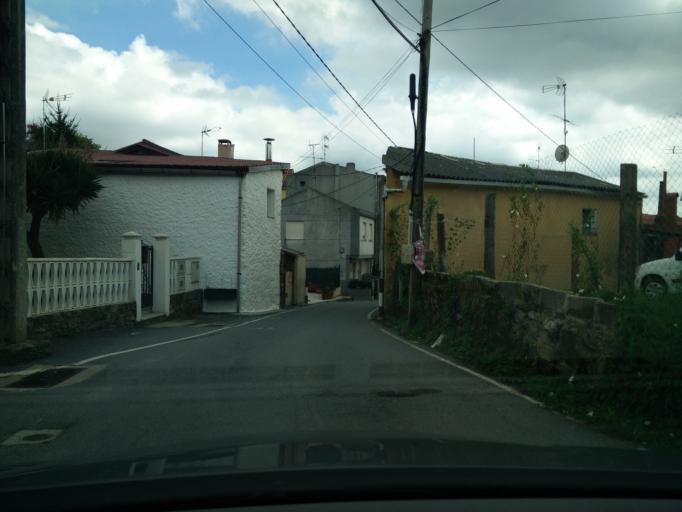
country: ES
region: Galicia
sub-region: Provincia da Coruna
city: Culleredo
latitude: 43.3154
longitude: -8.3951
